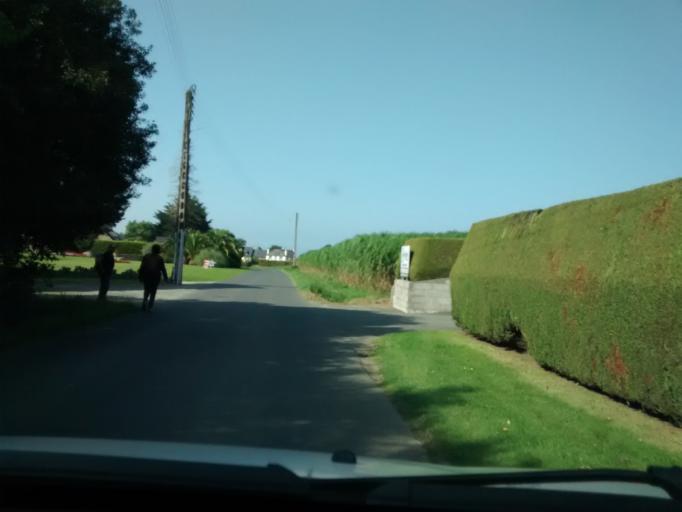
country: FR
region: Brittany
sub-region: Departement des Cotes-d'Armor
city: Penvenan
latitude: 48.8256
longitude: -3.3067
